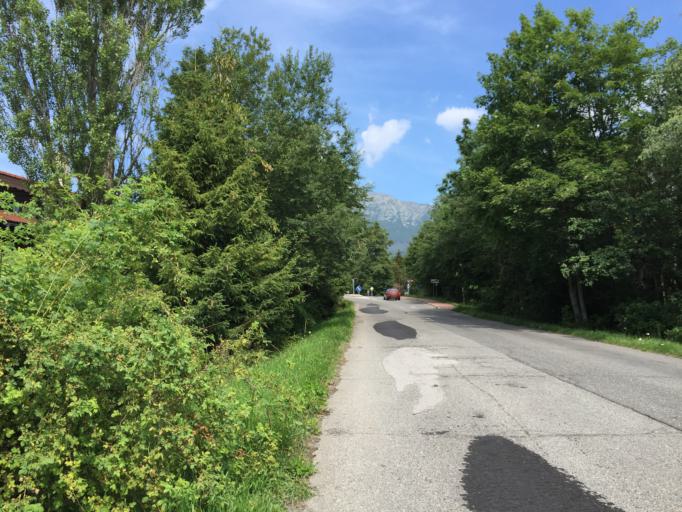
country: SK
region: Presovsky
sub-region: Okres Poprad
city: Vysoke Tatry
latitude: 49.1253
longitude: 20.2524
